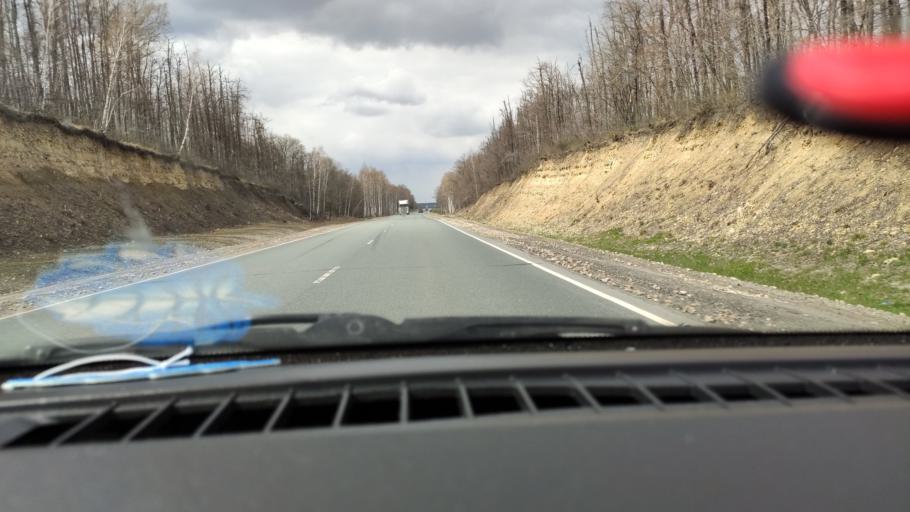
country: RU
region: Saratov
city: Vol'sk
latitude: 52.1118
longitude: 47.3306
